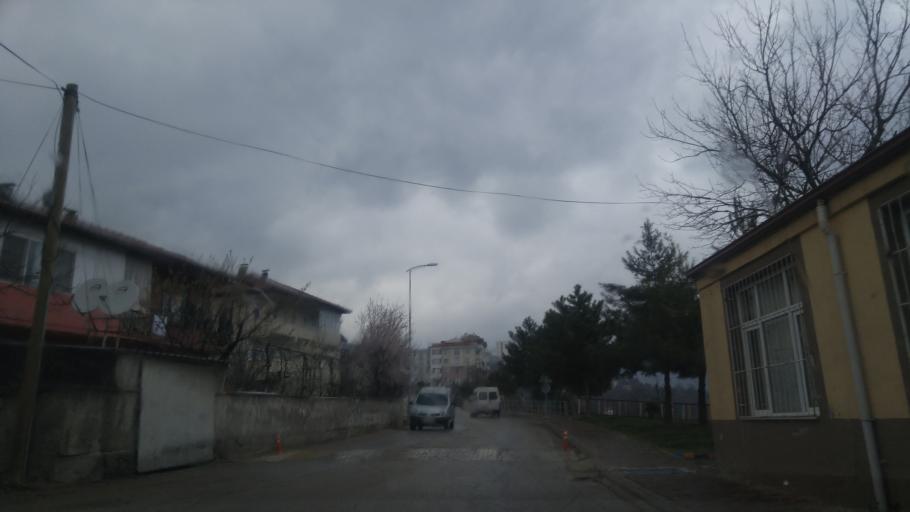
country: TR
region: Karabuk
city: Safranbolu
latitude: 41.2646
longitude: 32.6813
